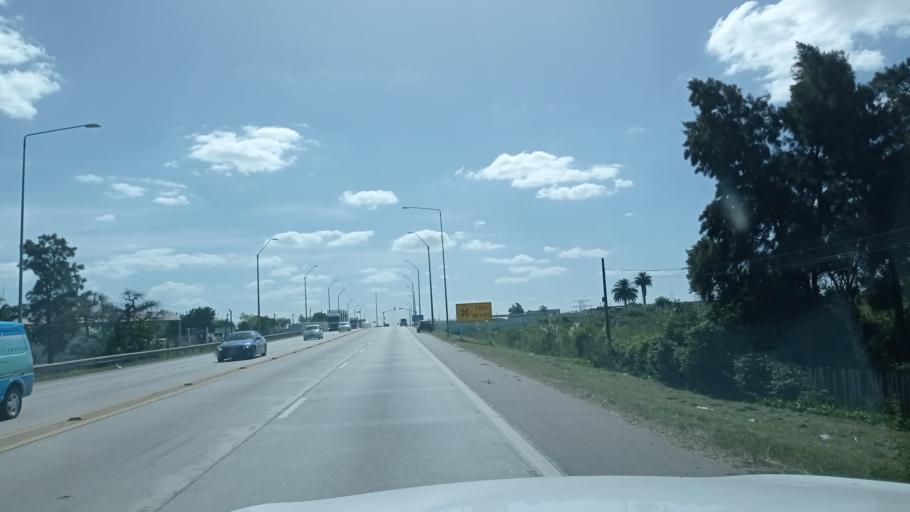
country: UY
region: Canelones
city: La Paz
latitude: -34.7865
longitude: -56.2198
